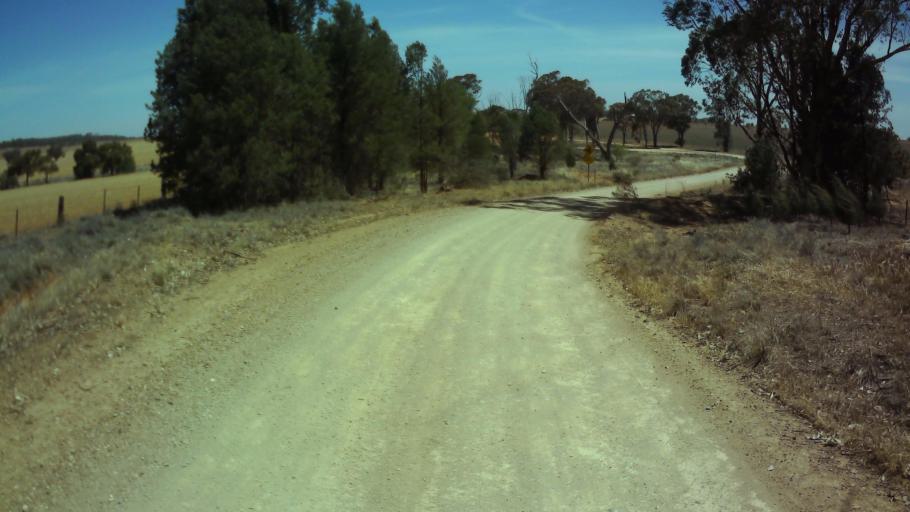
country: AU
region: New South Wales
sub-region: Weddin
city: Grenfell
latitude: -33.9219
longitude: 148.1783
